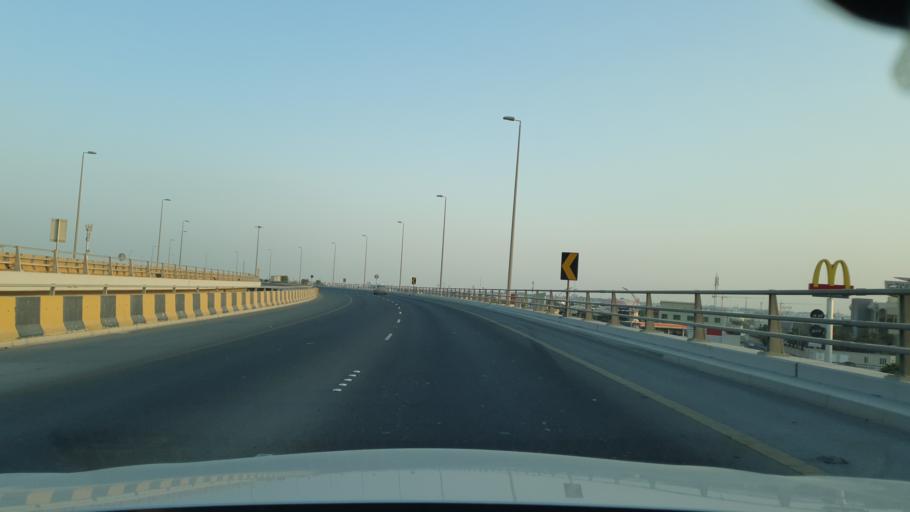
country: BH
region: Northern
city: Madinat `Isa
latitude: 26.1711
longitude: 50.5421
